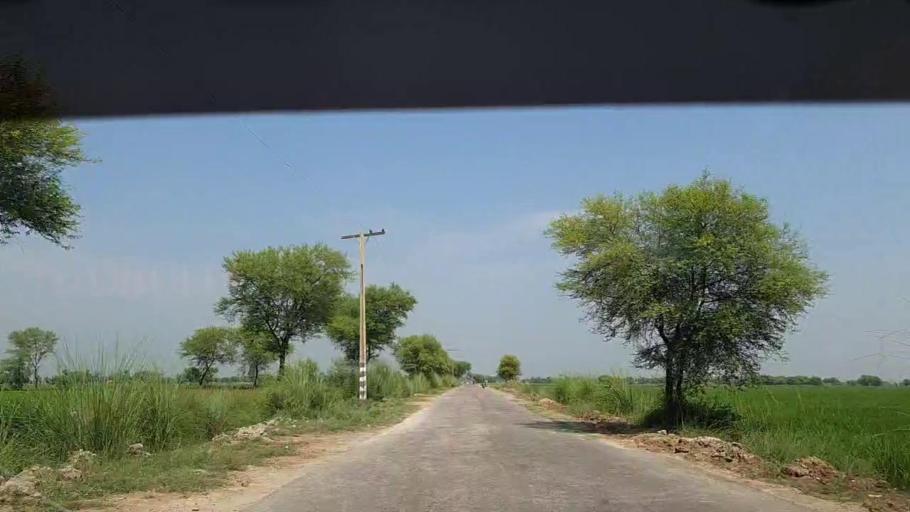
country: PK
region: Sindh
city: Thul
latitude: 28.1431
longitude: 68.7164
